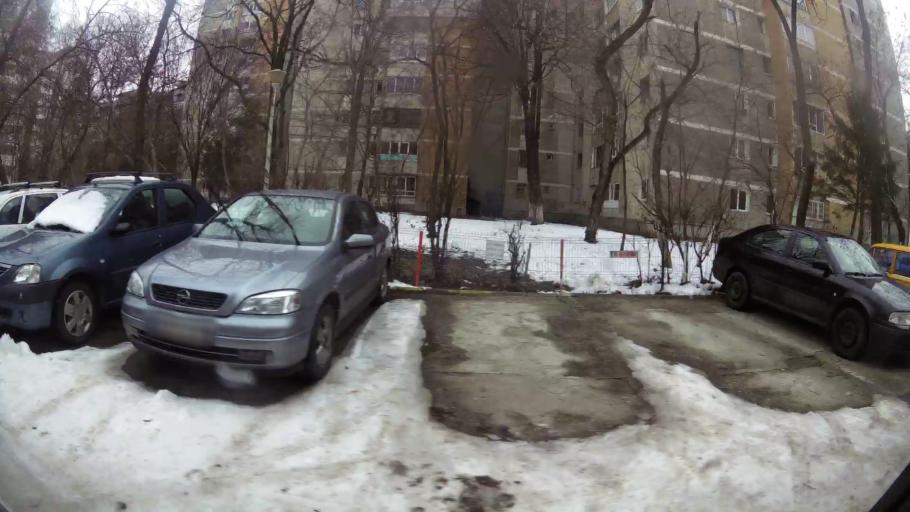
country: RO
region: Ilfov
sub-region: Comuna Chiajna
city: Rosu
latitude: 44.4204
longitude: 26.0416
